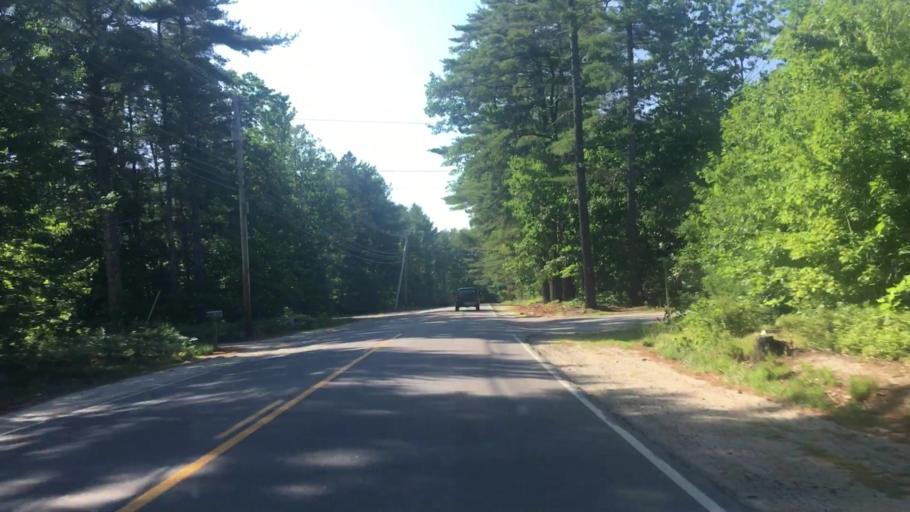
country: US
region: Maine
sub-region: York County
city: Hollis Center
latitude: 43.6889
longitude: -70.5934
